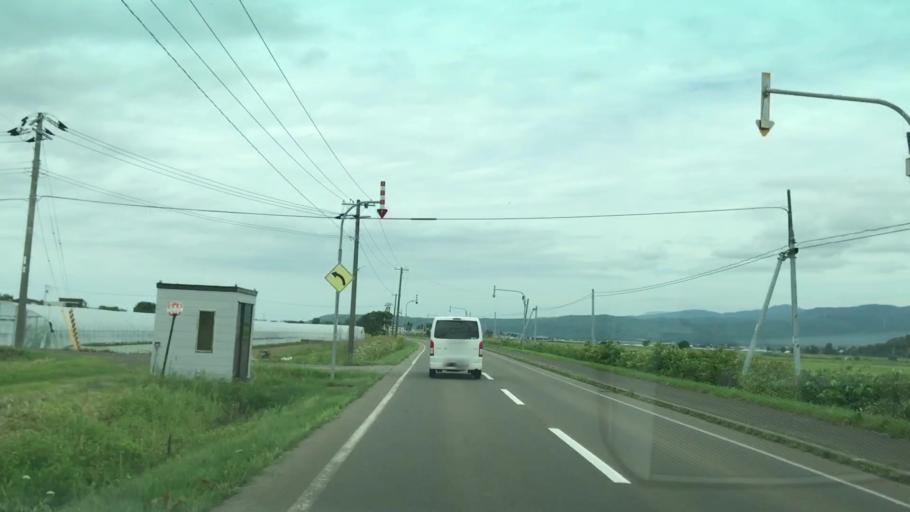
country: JP
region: Hokkaido
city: Iwanai
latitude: 42.9986
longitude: 140.5923
